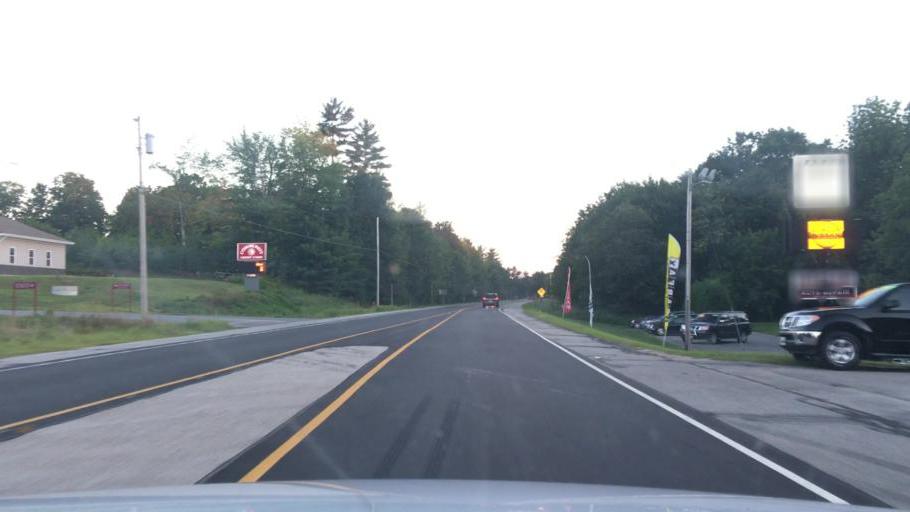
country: US
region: Maine
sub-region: Androscoggin County
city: Turner
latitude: 44.2500
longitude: -70.2594
